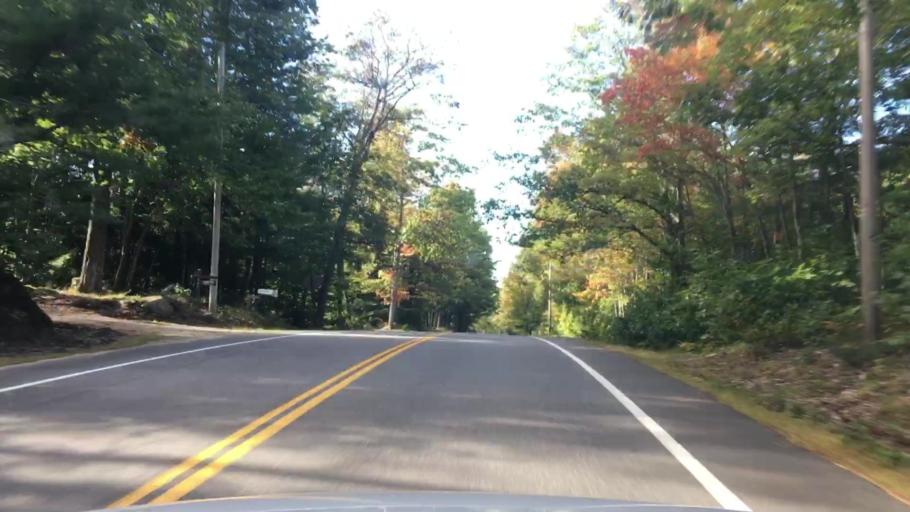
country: US
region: Maine
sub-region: Androscoggin County
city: Lisbon Falls
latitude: 43.9554
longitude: -70.0435
